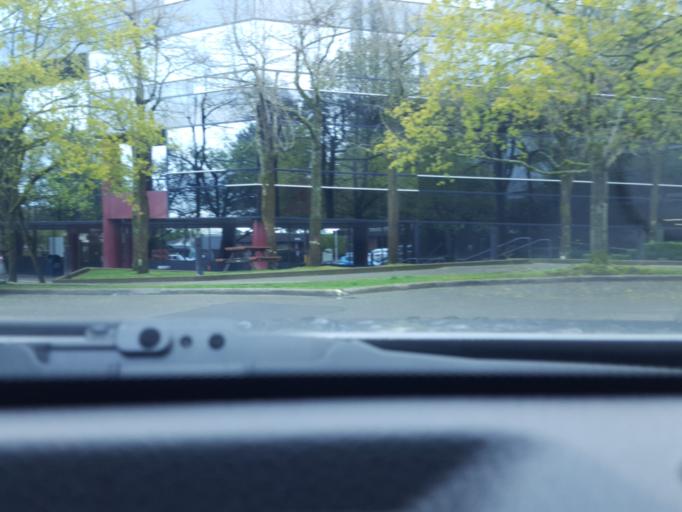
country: US
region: Washington
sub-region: King County
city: Shoreline
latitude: 47.6991
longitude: -122.3245
